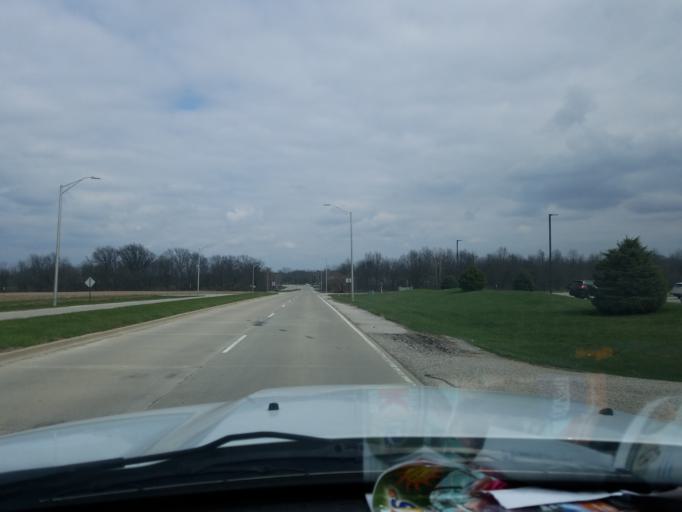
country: US
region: Indiana
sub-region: Sullivan County
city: Farmersburg
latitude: 39.3425
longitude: -87.3976
